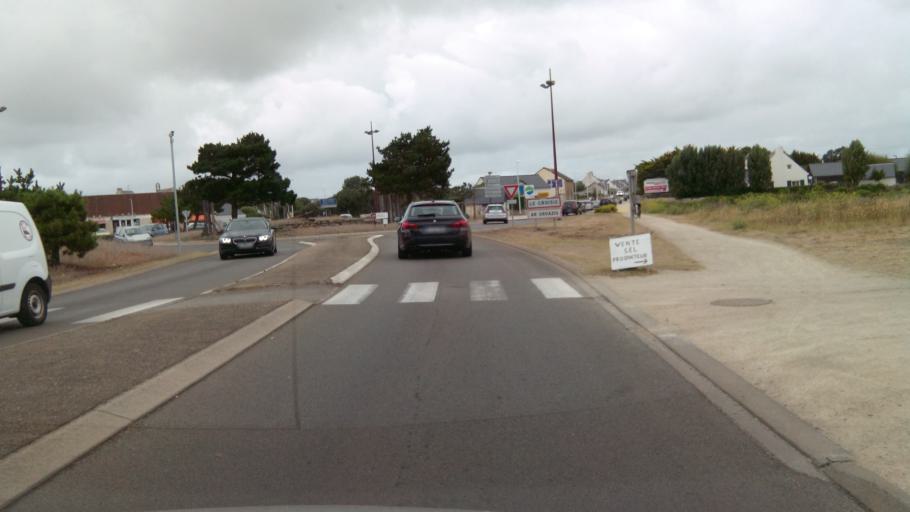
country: FR
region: Pays de la Loire
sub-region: Departement de la Loire-Atlantique
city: Le Croisic
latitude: 47.2826
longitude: -2.5024
